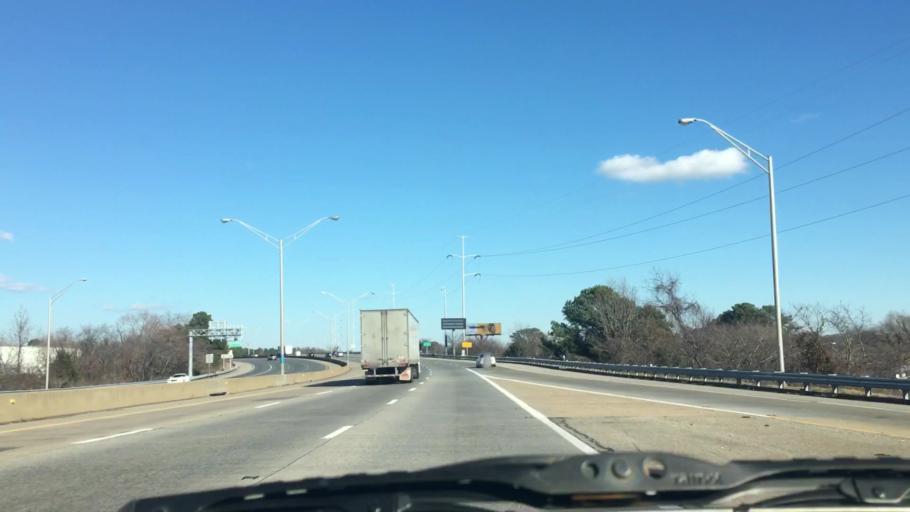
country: US
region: Virginia
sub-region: City of Newport News
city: Newport News
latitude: 36.9942
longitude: -76.4039
